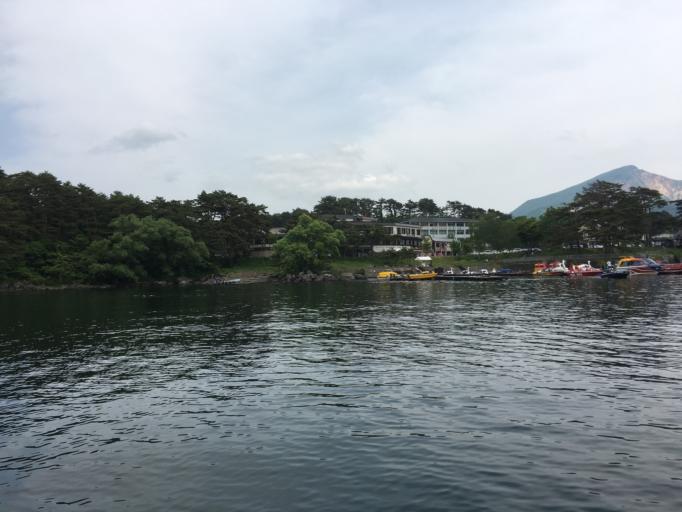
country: JP
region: Fukushima
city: Inawashiro
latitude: 37.6542
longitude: 140.0631
